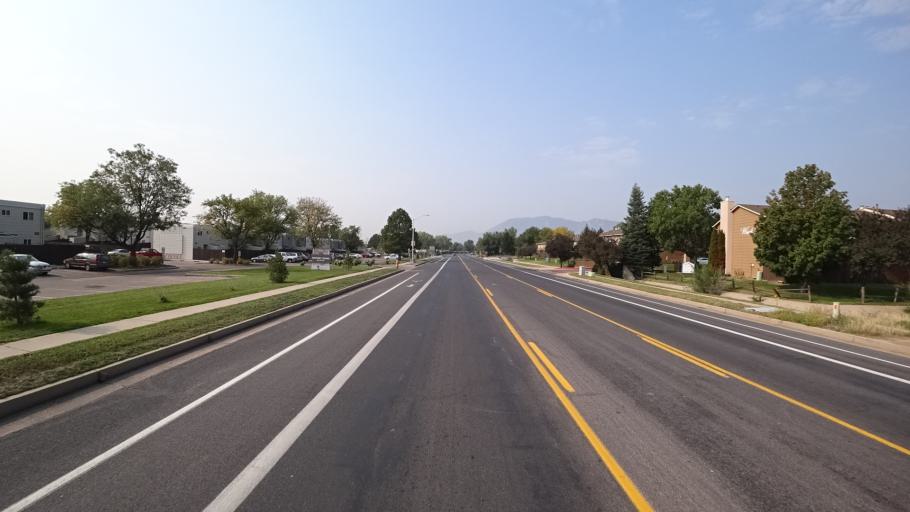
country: US
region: Colorado
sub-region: El Paso County
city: Stratmoor
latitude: 38.8025
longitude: -104.7605
